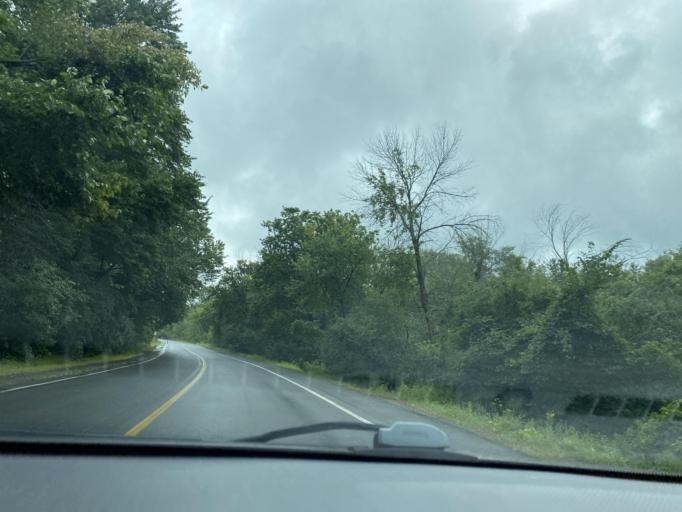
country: CA
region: Quebec
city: Baie-D'Urfe
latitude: 45.4386
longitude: -73.9075
